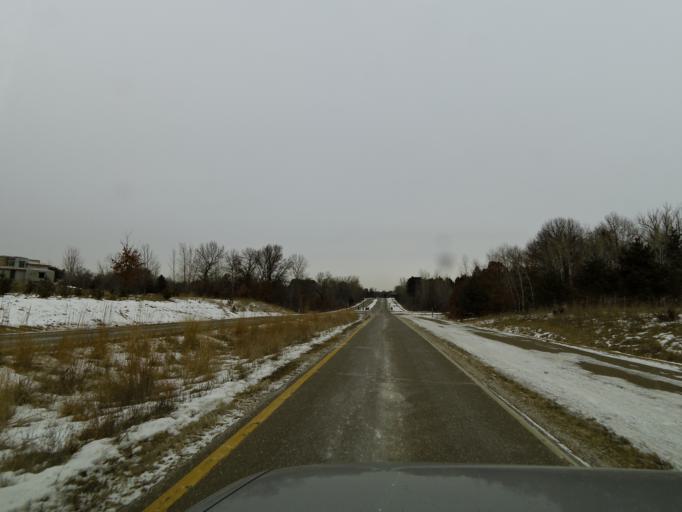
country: US
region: Minnesota
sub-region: Washington County
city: Lake Elmo
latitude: 44.9676
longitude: -92.9033
